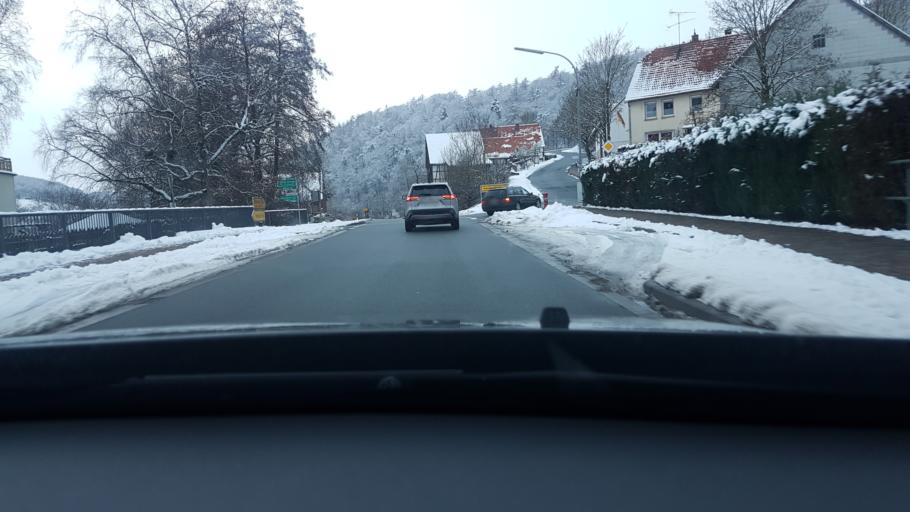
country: DE
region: Hesse
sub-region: Regierungsbezirk Kassel
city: Korbach
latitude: 51.3278
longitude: 8.8262
